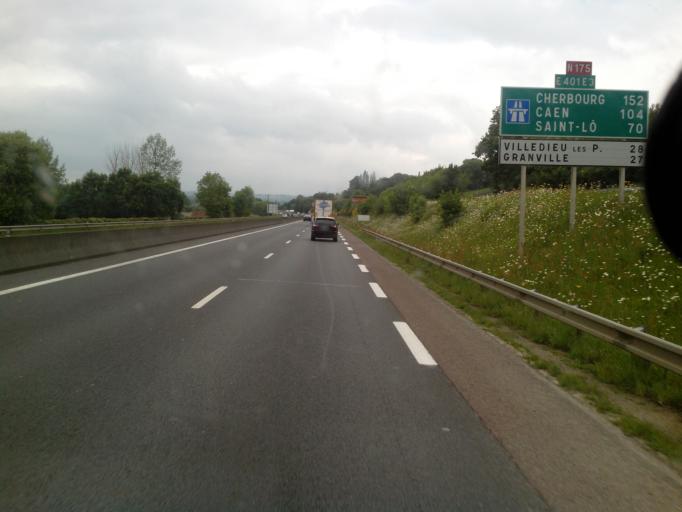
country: FR
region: Lower Normandy
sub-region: Departement de la Manche
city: Avranches
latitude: 48.6778
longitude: -1.3722
